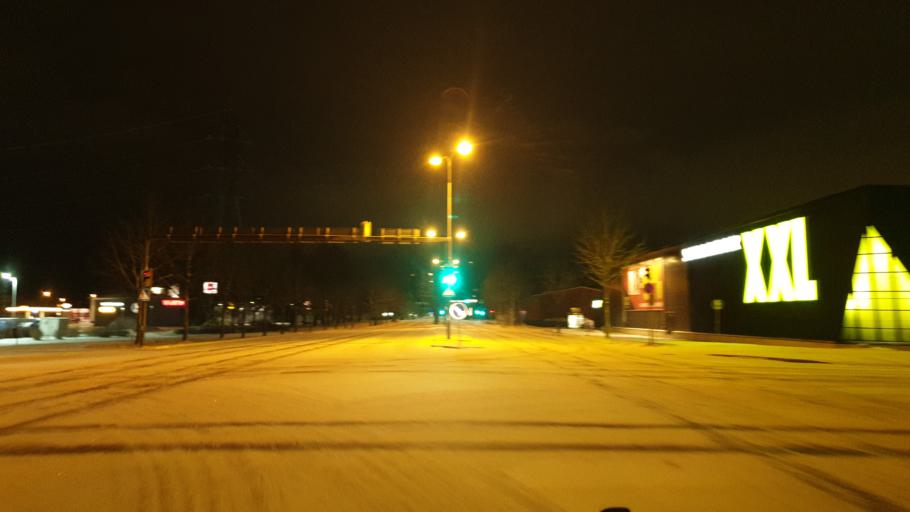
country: FI
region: Northern Ostrobothnia
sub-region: Oulu
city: Oulu
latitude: 64.9963
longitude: 25.4646
